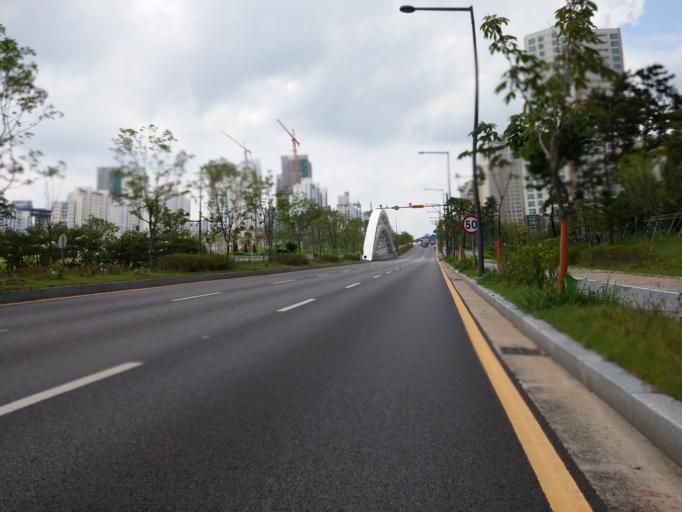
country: KR
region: Chungcheongnam-do
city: Gongju
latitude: 36.4990
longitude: 127.2534
